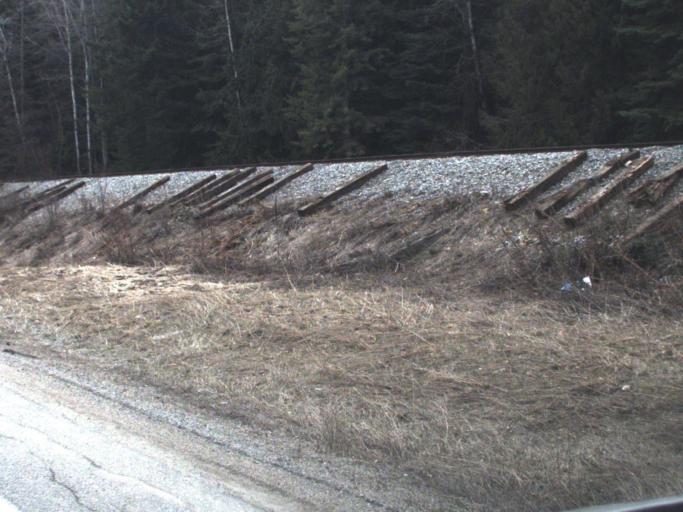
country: US
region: Washington
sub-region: Pend Oreille County
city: Newport
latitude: 48.2391
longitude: -117.2295
